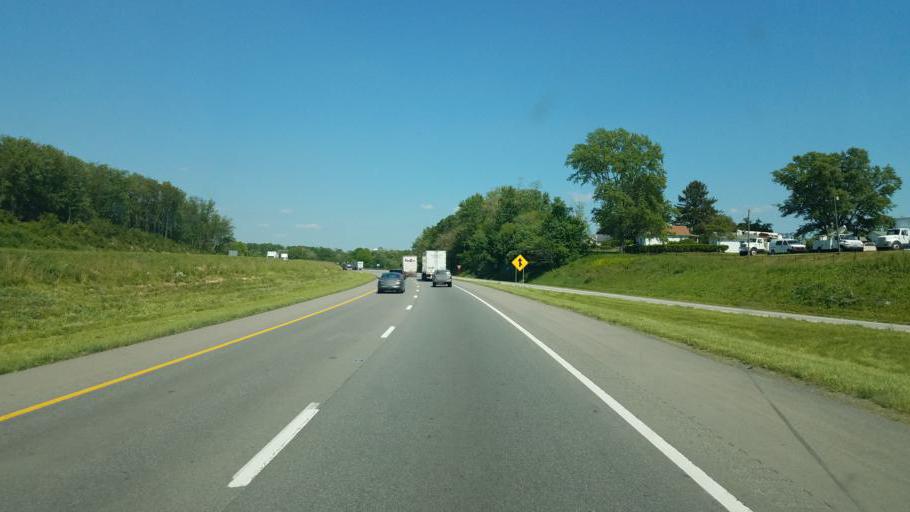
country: US
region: Ohio
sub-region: Muskingum County
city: Pleasant Grove
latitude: 39.9496
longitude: -81.9588
